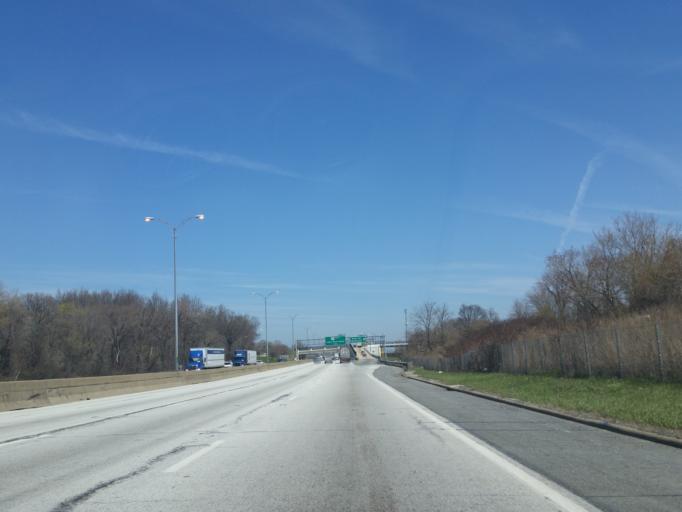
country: US
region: Ohio
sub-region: Cuyahoga County
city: Bratenahl
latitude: 41.5482
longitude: -81.6091
